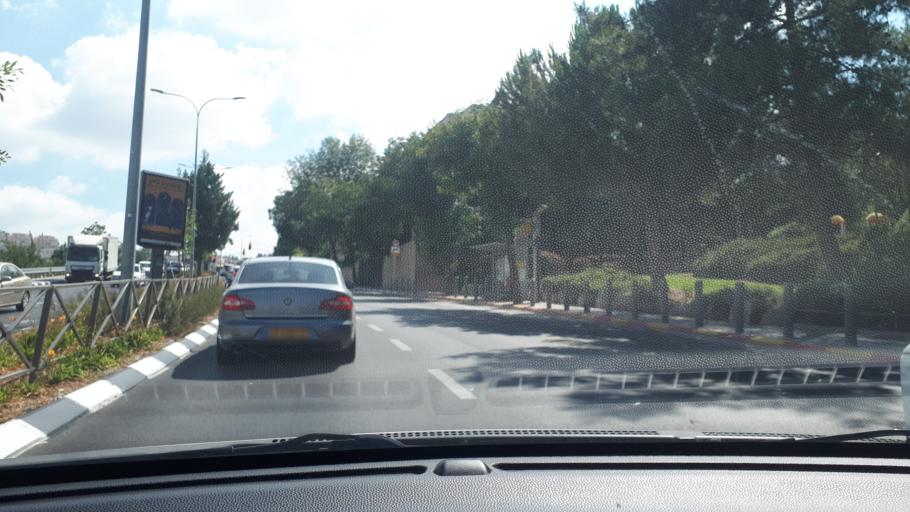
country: PS
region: West Bank
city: Hizma
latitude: 31.8284
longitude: 35.2465
